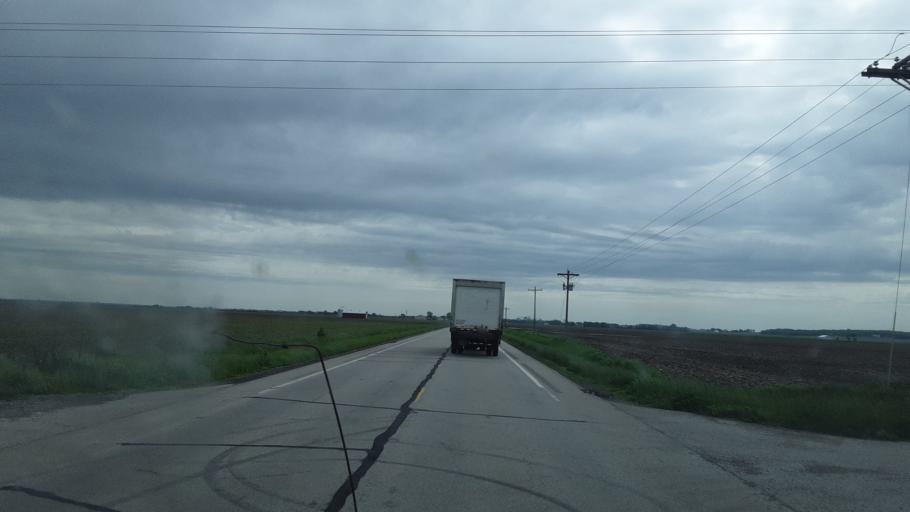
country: US
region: Illinois
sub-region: Mason County
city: Mason City
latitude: 40.3046
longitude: -89.7151
